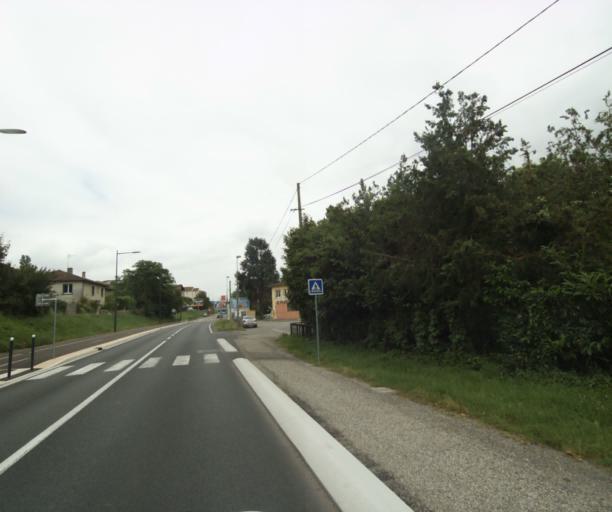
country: FR
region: Midi-Pyrenees
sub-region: Departement du Tarn-et-Garonne
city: Montauban
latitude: 44.0035
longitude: 1.3644
